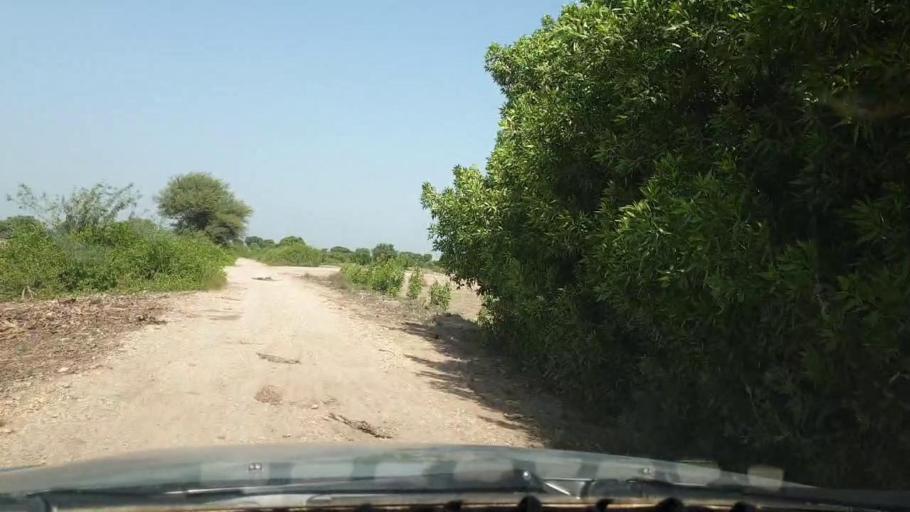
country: PK
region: Sindh
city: Tando Muhammad Khan
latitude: 25.1747
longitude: 68.6318
